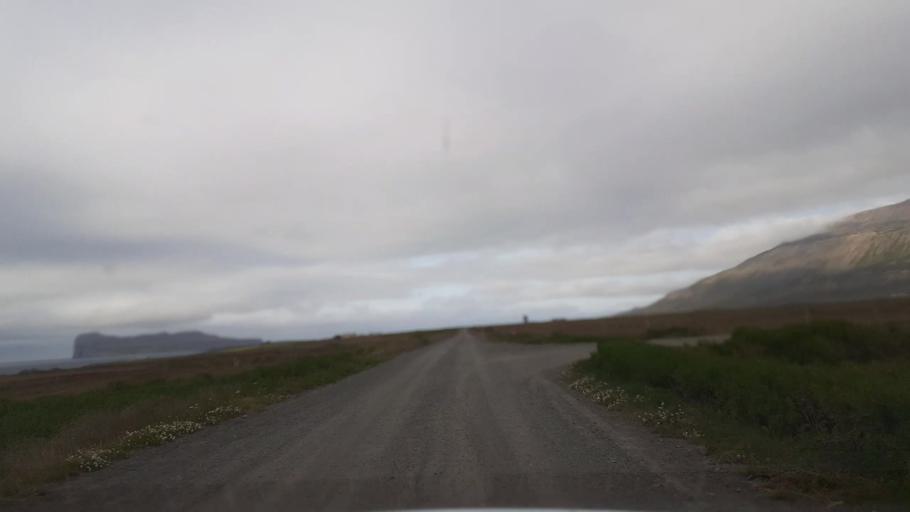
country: IS
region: Northwest
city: Saudarkrokur
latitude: 65.9022
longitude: -19.4219
